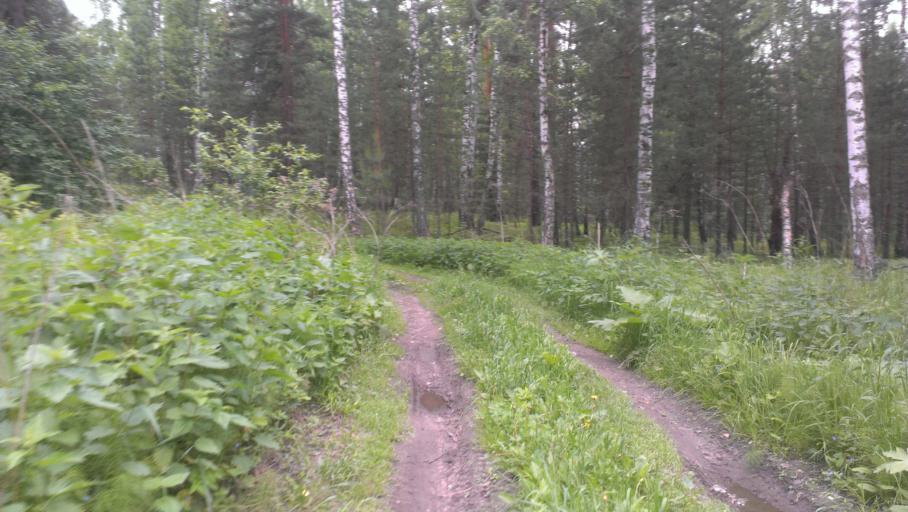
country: RU
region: Altai Krai
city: Sannikovo
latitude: 53.3439
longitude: 84.0442
